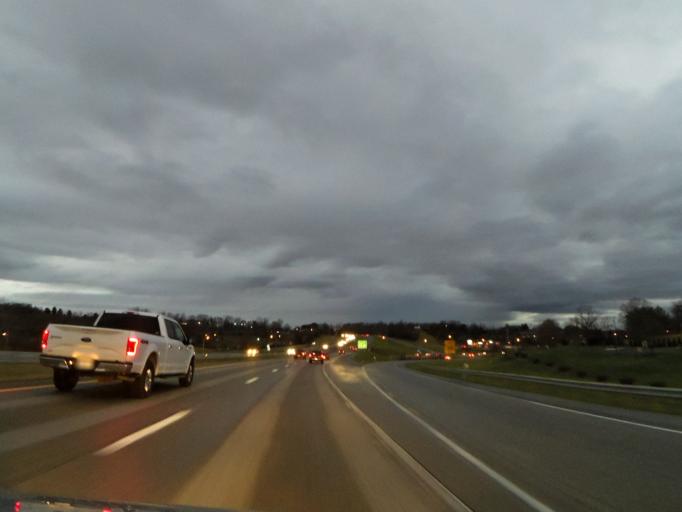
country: US
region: Tennessee
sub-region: Washington County
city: Oak Grove
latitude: 36.3752
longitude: -82.4254
